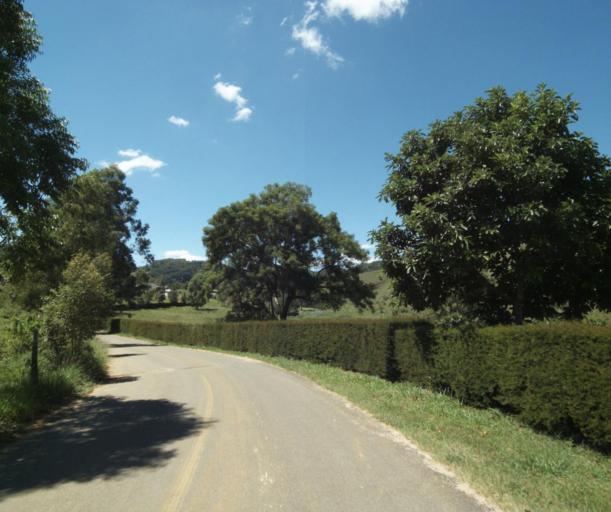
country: BR
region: Minas Gerais
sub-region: Espera Feliz
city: Espera Feliz
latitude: -20.6239
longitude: -41.8274
